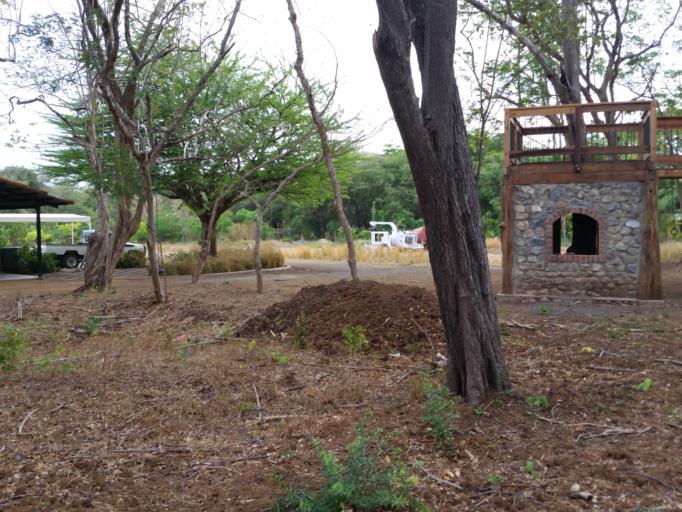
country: NI
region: Rivas
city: Tola
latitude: 11.4411
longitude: -86.0829
